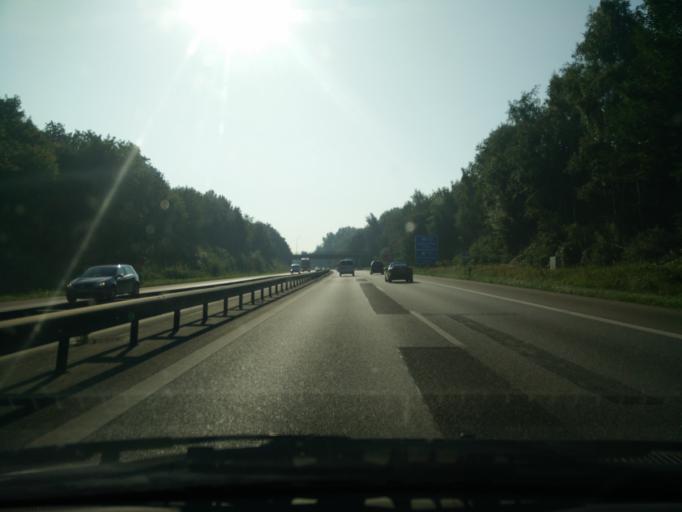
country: DE
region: Hamburg
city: Eidelstedt
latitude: 53.6246
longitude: 9.8873
